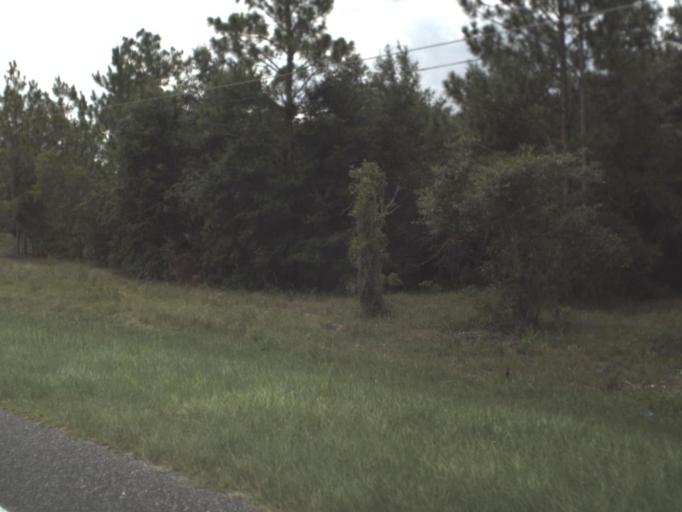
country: US
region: Florida
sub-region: Levy County
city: East Bronson
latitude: 29.4323
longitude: -82.6077
